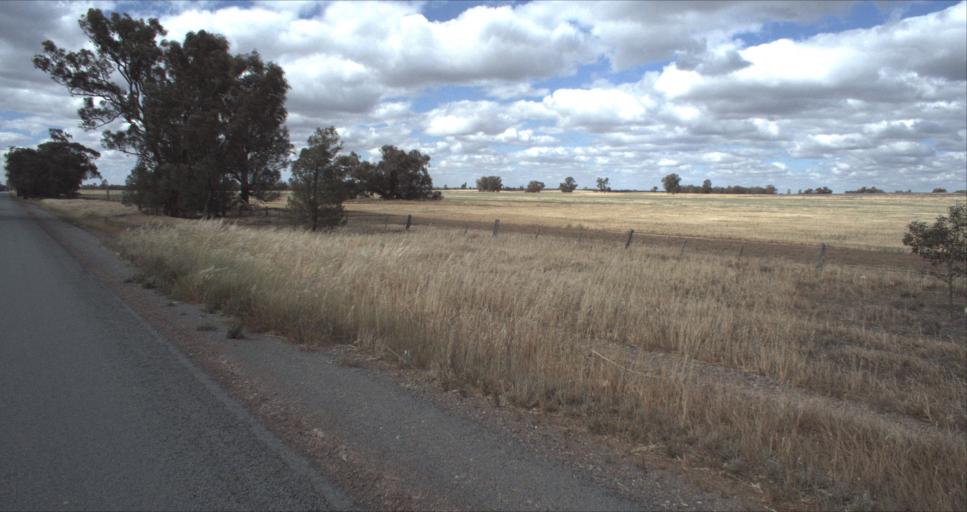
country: AU
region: New South Wales
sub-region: Leeton
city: Leeton
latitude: -34.6800
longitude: 146.3458
